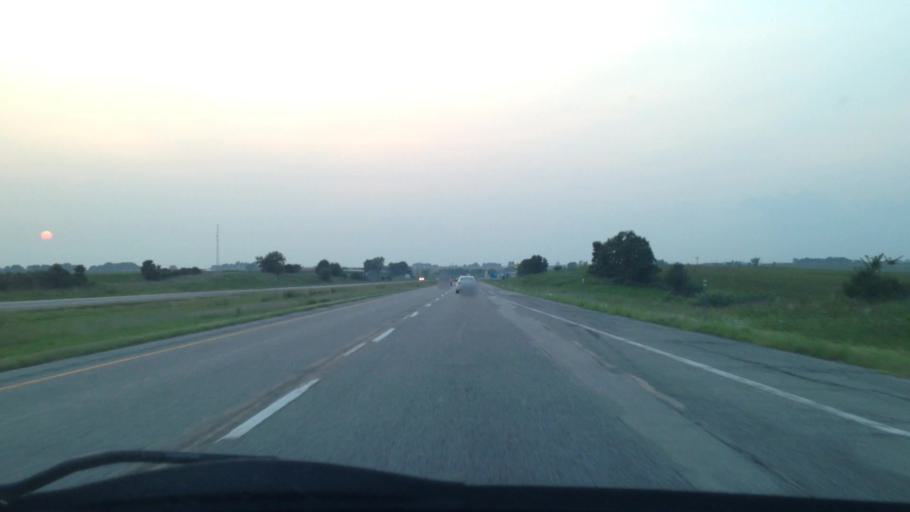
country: US
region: Iowa
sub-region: Benton County
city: Urbana
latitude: 42.2318
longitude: -91.8720
